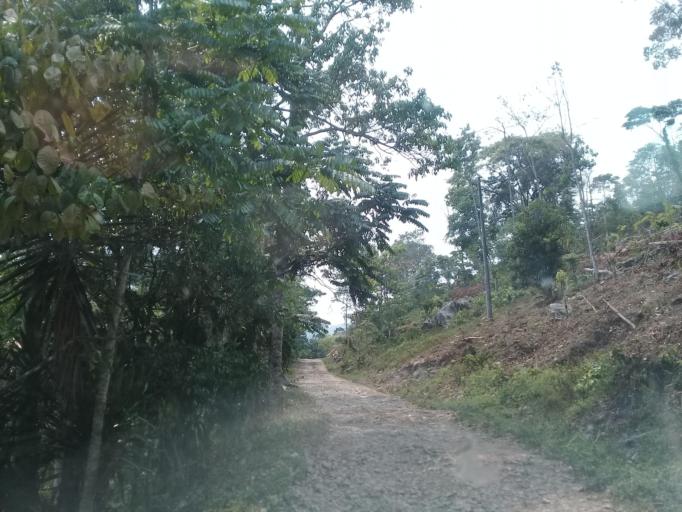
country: MX
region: Veracruz
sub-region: Tezonapa
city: Laguna Chica (Pueblo Nuevo)
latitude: 18.5806
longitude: -96.7541
